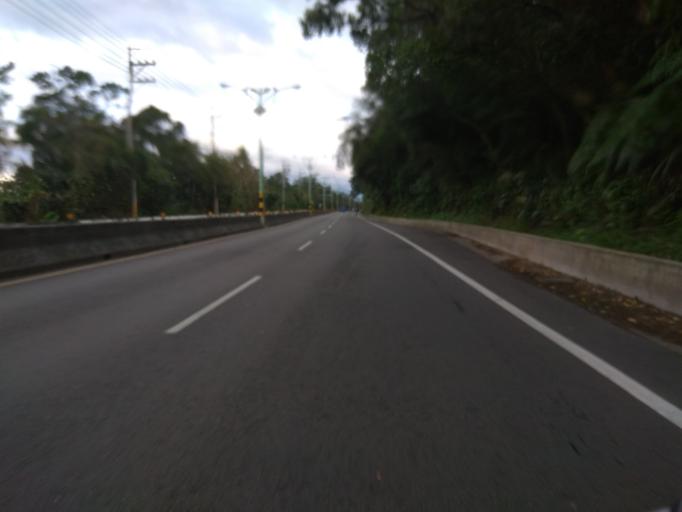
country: TW
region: Taiwan
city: Daxi
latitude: 24.8474
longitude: 121.2081
